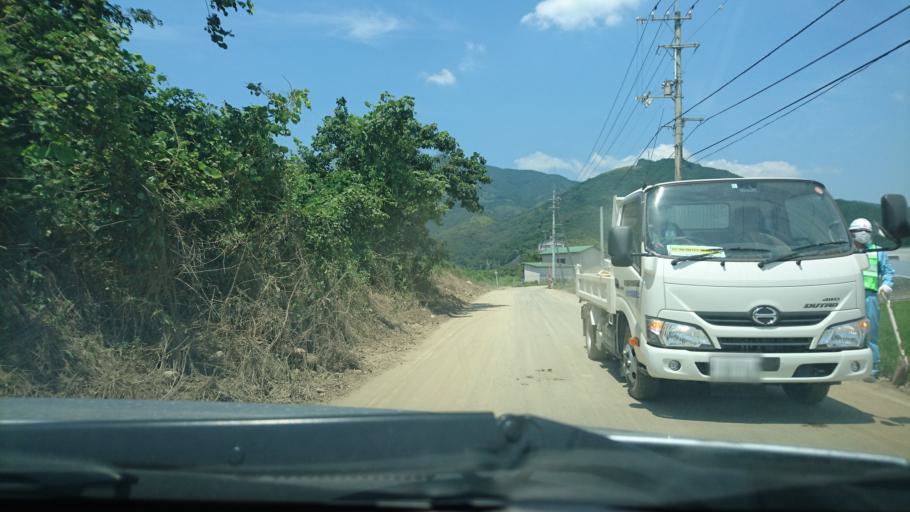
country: JP
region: Ehime
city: Ozu
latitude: 33.5352
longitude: 132.5672
